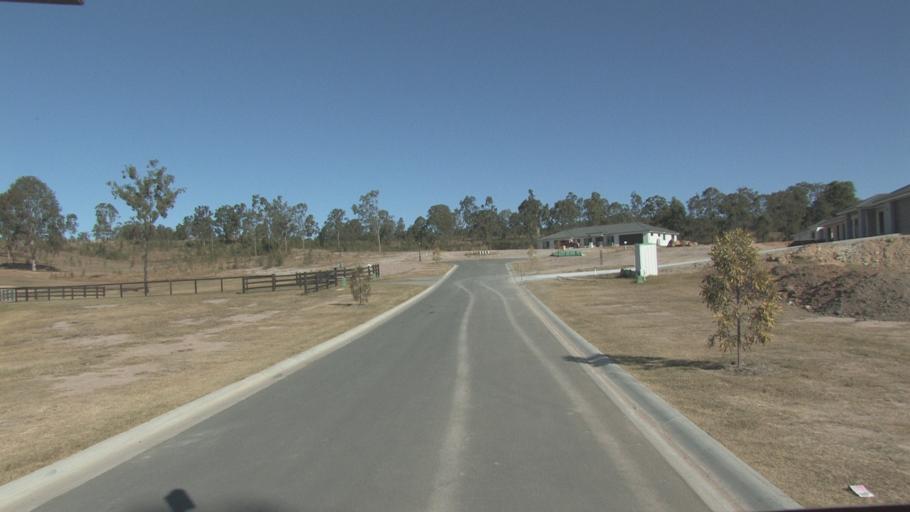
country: AU
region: Queensland
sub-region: Logan
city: Cedar Vale
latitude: -27.8749
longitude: 153.0446
